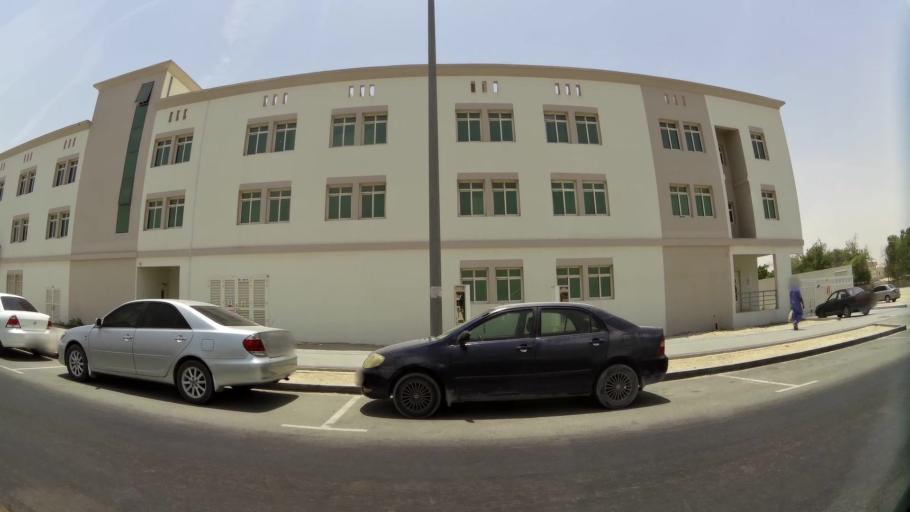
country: AE
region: Ash Shariqah
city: Sharjah
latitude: 25.2684
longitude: 55.4277
